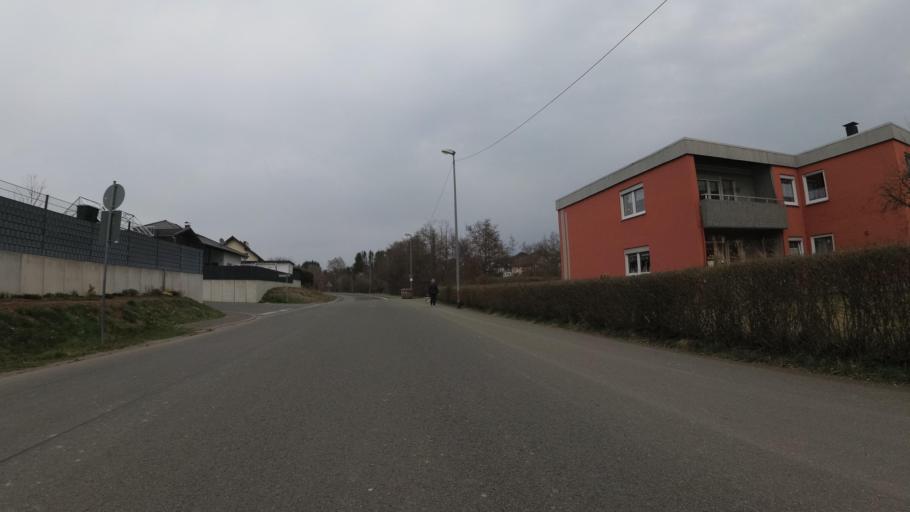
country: DE
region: Rheinland-Pfalz
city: Birkenfeld
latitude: 49.6556
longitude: 7.1693
